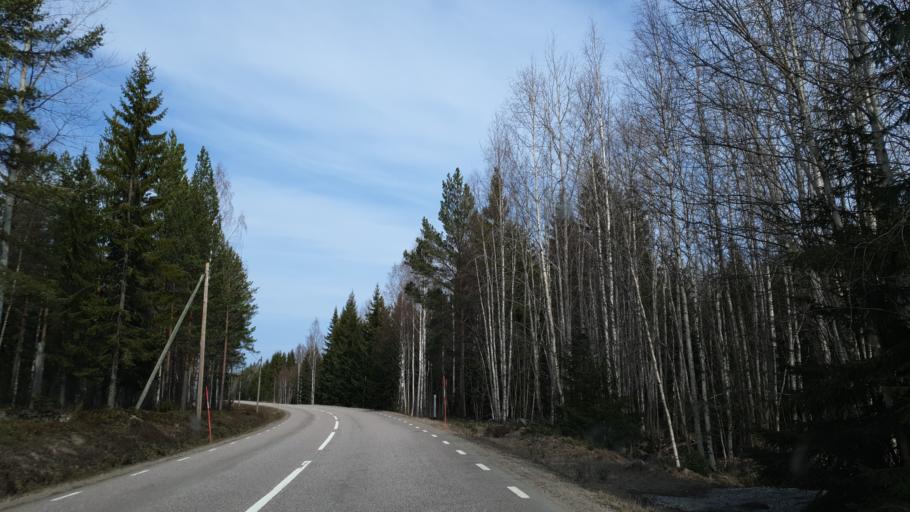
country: SE
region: Gaevleborg
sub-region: Gavle Kommun
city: Norrsundet
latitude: 60.9854
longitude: 17.0778
